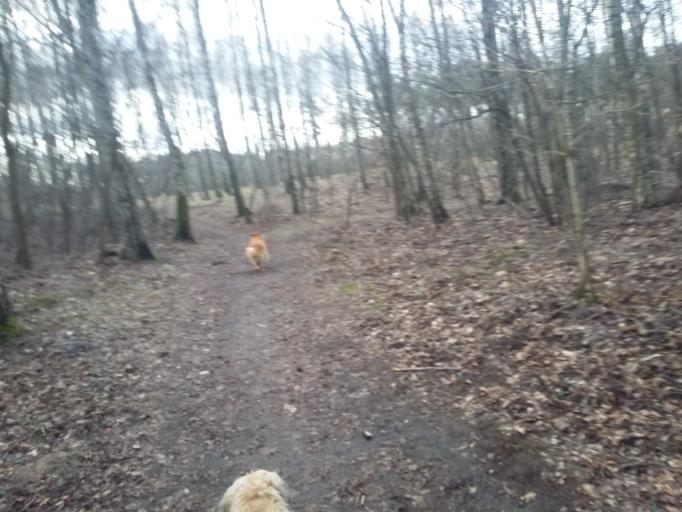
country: PL
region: Lodz Voivodeship
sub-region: Powiat pabianicki
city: Ksawerow
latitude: 51.7282
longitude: 19.4180
